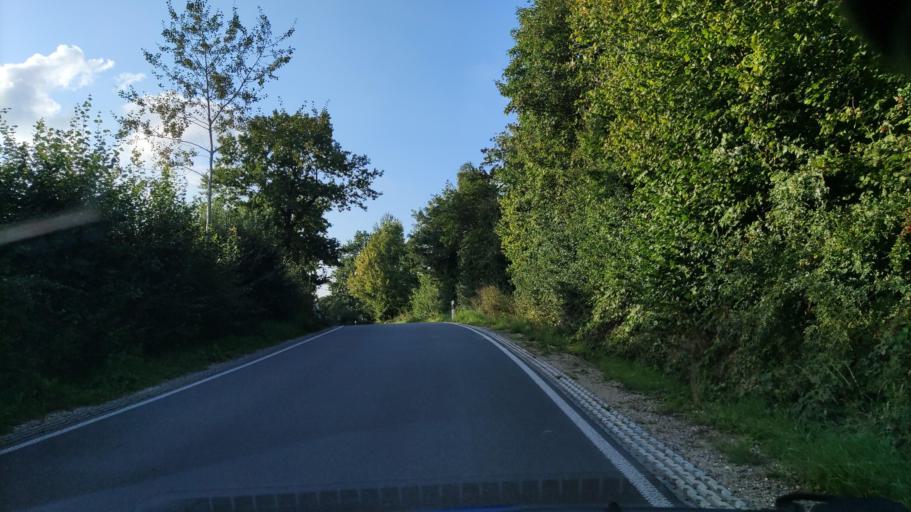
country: DE
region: Schleswig-Holstein
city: Bosdorf
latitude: 54.0990
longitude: 10.4819
